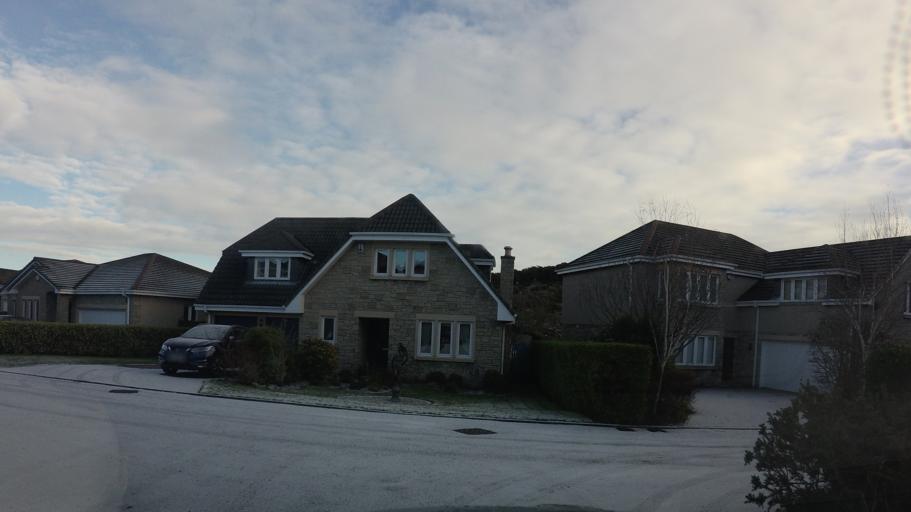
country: GB
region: Scotland
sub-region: Fife
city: North Queensferry
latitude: 56.0128
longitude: -3.3911
